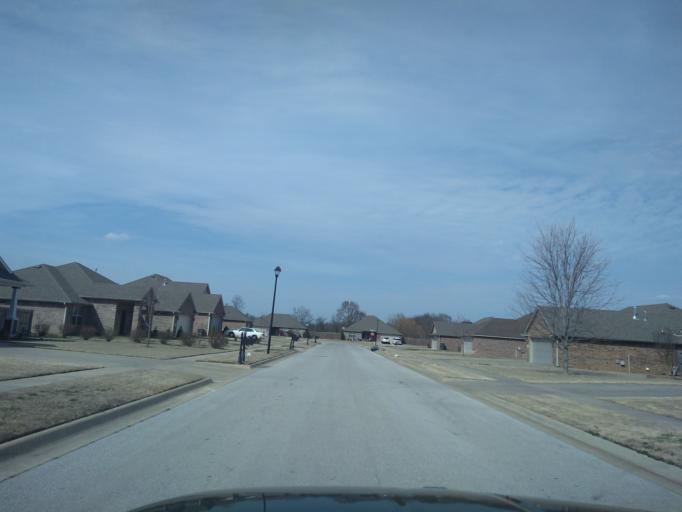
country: US
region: Arkansas
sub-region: Washington County
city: Farmington
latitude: 36.0699
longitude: -94.2461
